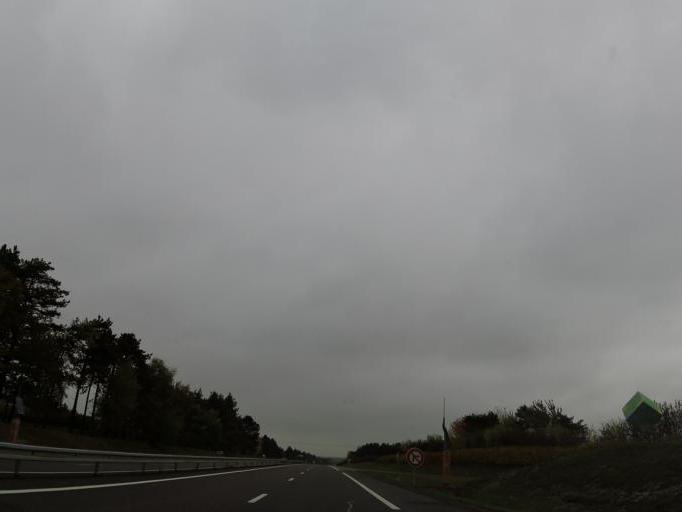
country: FR
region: Champagne-Ardenne
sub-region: Departement de la Marne
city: Courtisols
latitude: 49.0275
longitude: 4.5224
